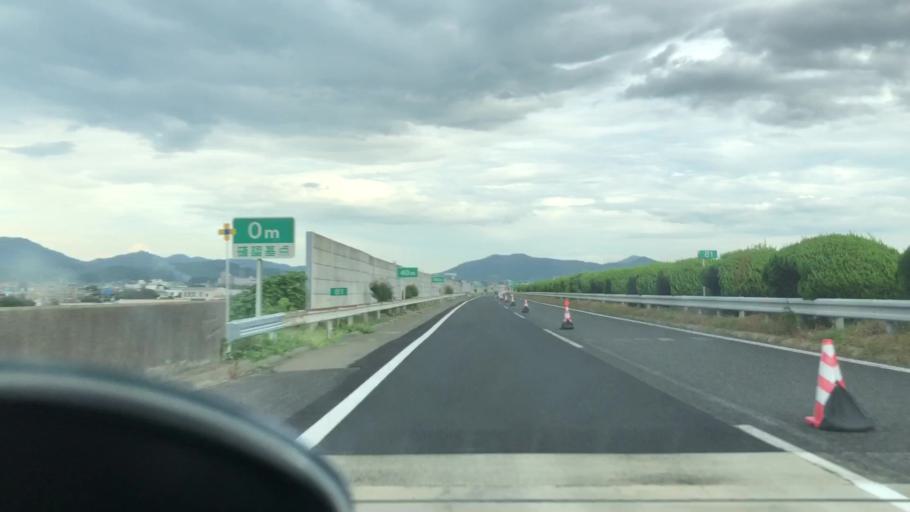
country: JP
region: Hyogo
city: Himeji
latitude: 34.9529
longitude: 134.7445
